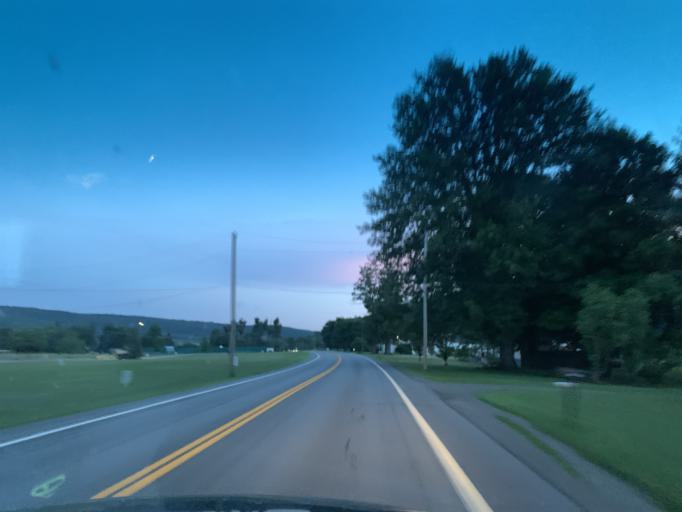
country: US
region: New York
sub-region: Chenango County
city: New Berlin
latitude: 42.5818
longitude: -75.3367
